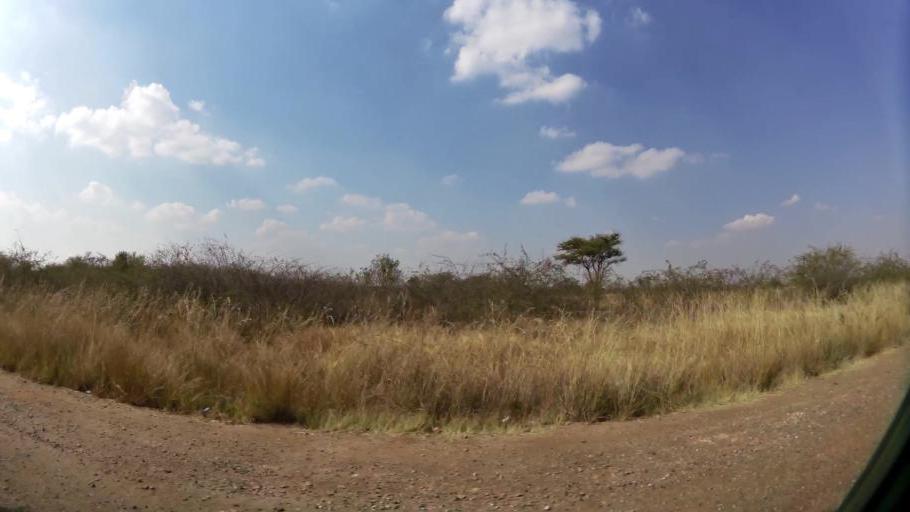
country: ZA
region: North-West
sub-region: Bojanala Platinum District Municipality
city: Rustenburg
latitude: -25.5114
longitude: 27.1001
